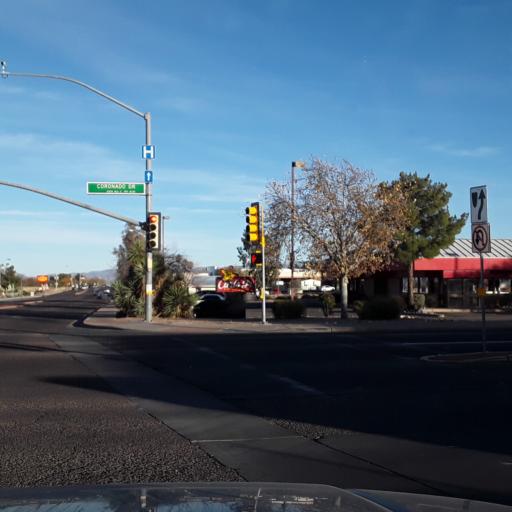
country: US
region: Arizona
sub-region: Cochise County
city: Sierra Vista
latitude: 31.5545
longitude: -110.2778
